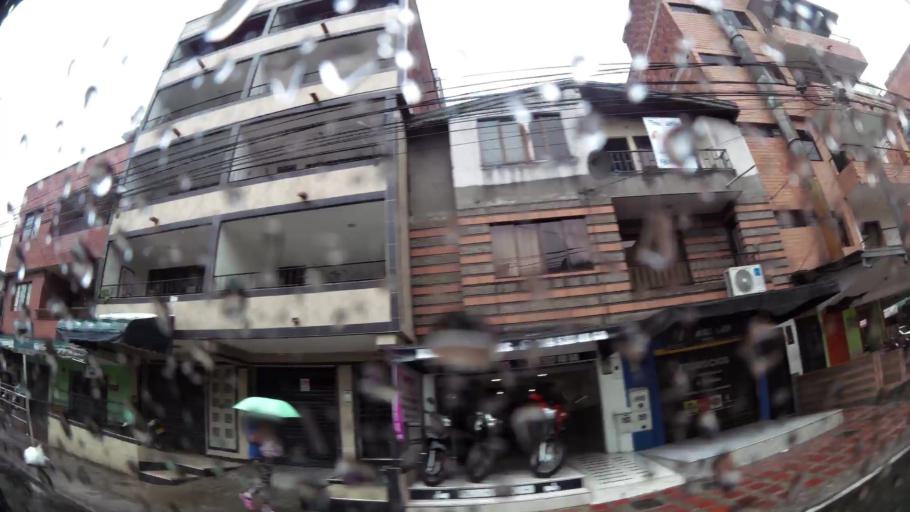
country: CO
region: Antioquia
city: Itagui
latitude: 6.1856
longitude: -75.5959
